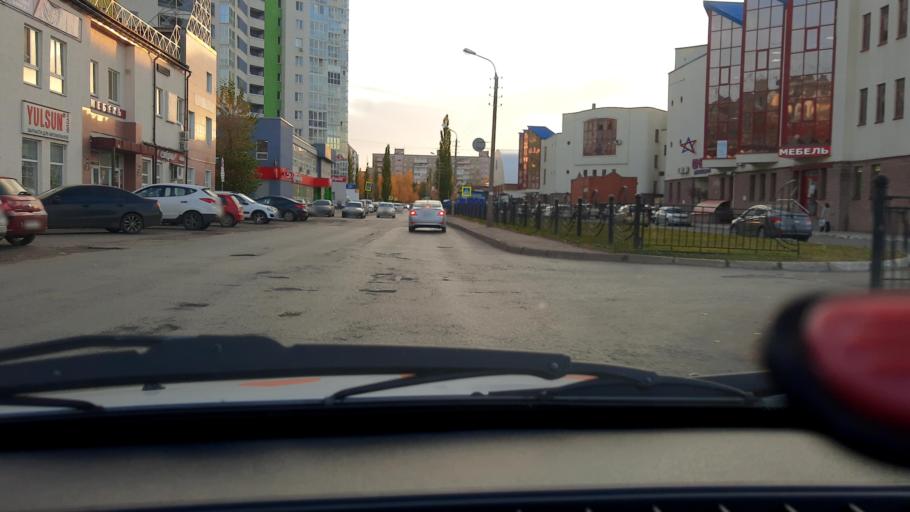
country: RU
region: Bashkortostan
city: Ufa
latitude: 54.7705
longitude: 56.0617
